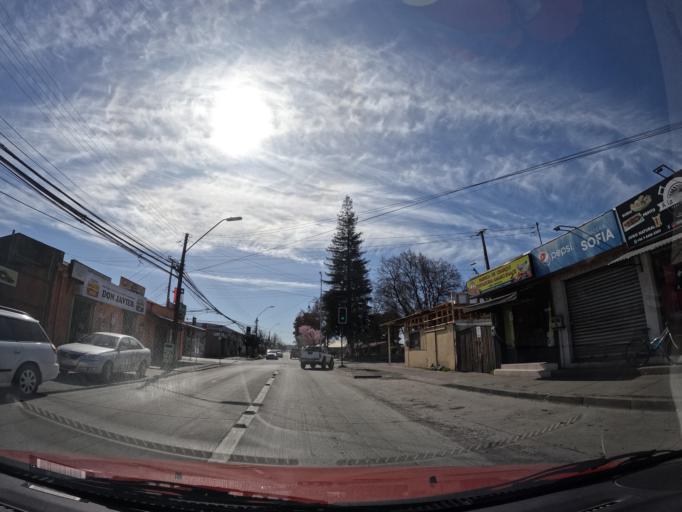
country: CL
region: Biobio
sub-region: Provincia de Biobio
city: Cabrero
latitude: -37.0367
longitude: -72.4005
